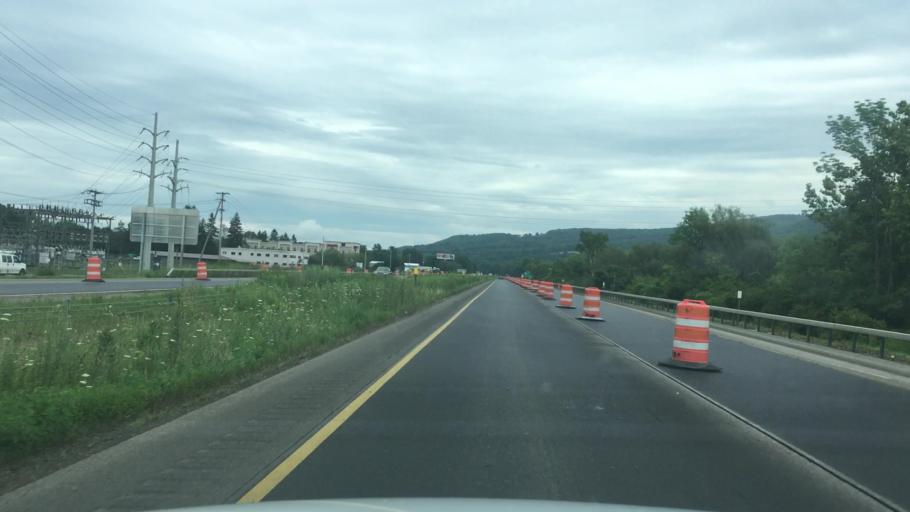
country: US
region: New York
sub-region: Otsego County
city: West End
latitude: 42.4433
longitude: -75.0932
